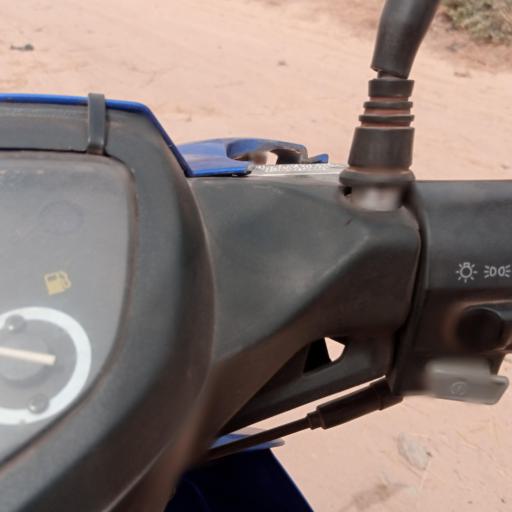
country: BF
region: Centre
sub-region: Kadiogo Province
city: Ouagadougou
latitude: 12.3441
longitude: -1.6750
